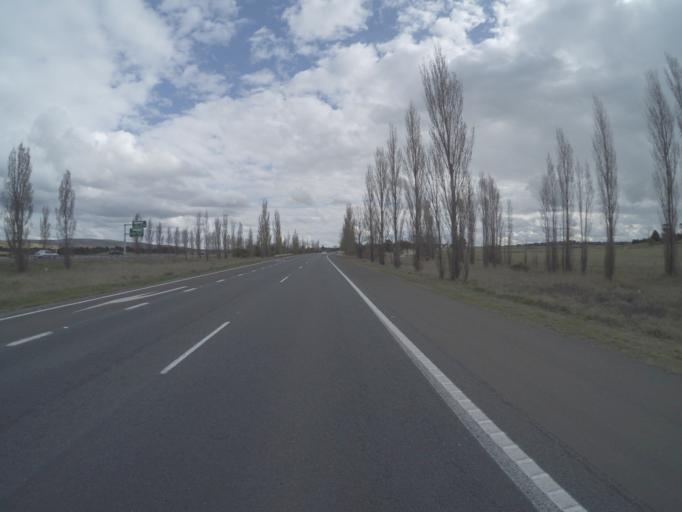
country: AU
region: New South Wales
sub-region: Goulburn Mulwaree
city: Goulburn
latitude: -34.7961
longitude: 149.6157
